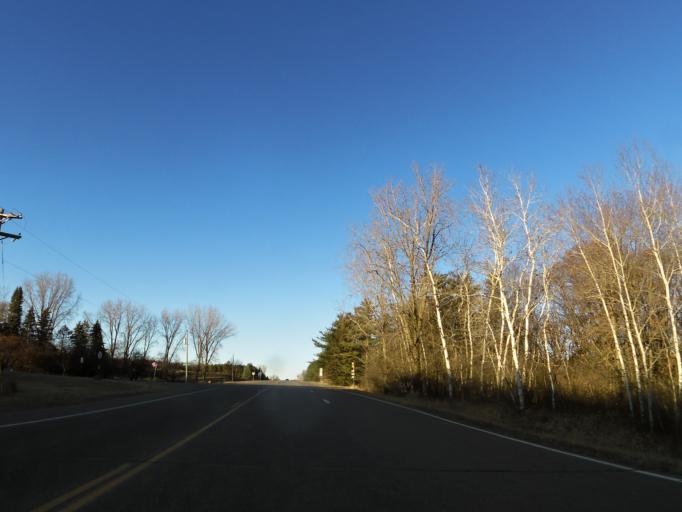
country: US
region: Minnesota
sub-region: Washington County
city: Stillwater
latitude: 45.1040
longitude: -92.8332
